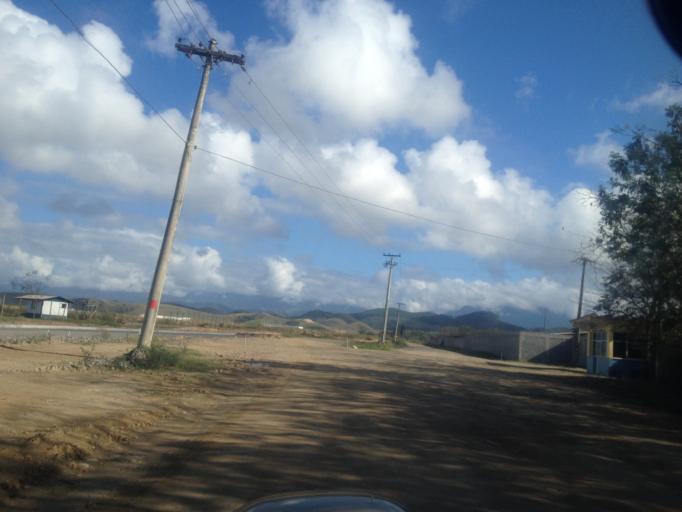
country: BR
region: Rio de Janeiro
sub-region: Resende
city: Resende
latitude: -22.4371
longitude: -44.3712
